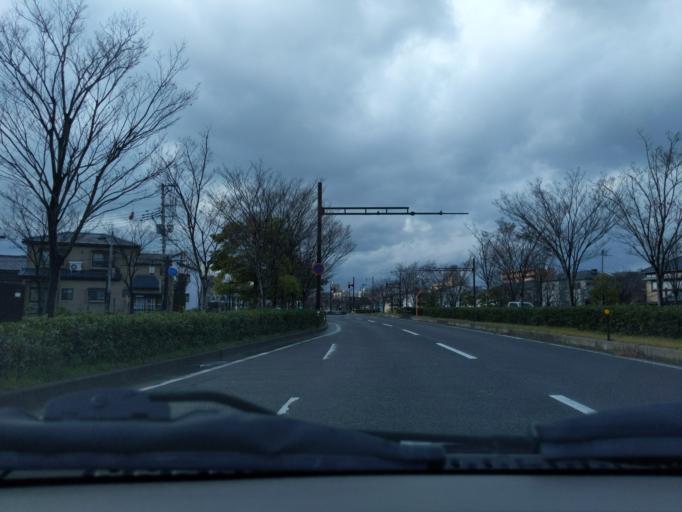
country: JP
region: Niigata
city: Niigata-shi
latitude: 37.9254
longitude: 139.0518
